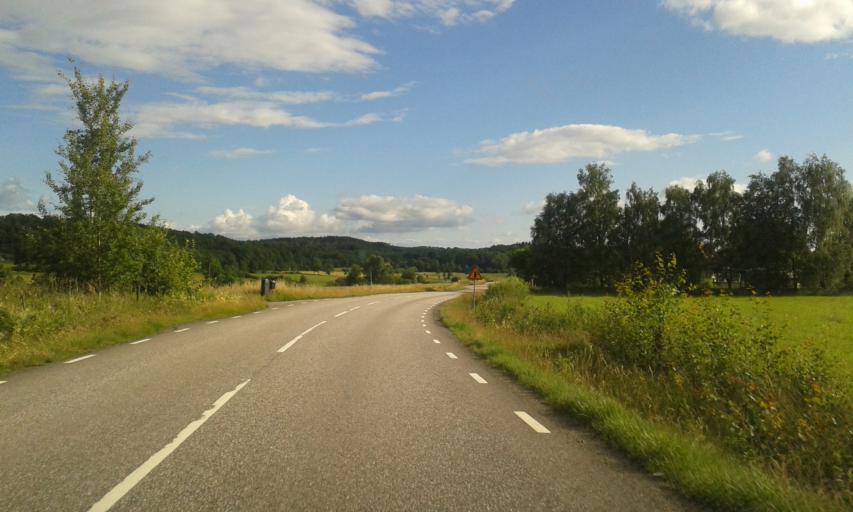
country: SE
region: Vaestra Goetaland
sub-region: Ale Kommun
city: Nodinge-Nol
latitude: 57.9367
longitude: 12.0431
